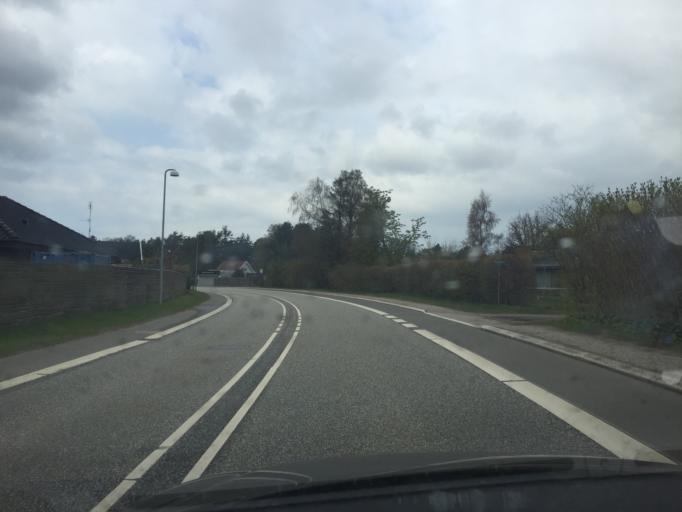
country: DK
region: Capital Region
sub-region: Halsnaes Kommune
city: Frederiksvaerk
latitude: 56.0030
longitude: 12.0115
